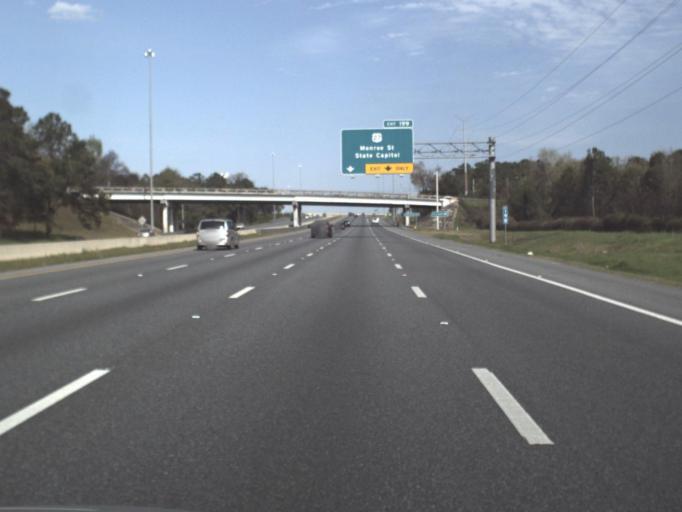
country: US
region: Florida
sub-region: Leon County
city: Tallahassee
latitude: 30.4799
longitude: -84.3200
